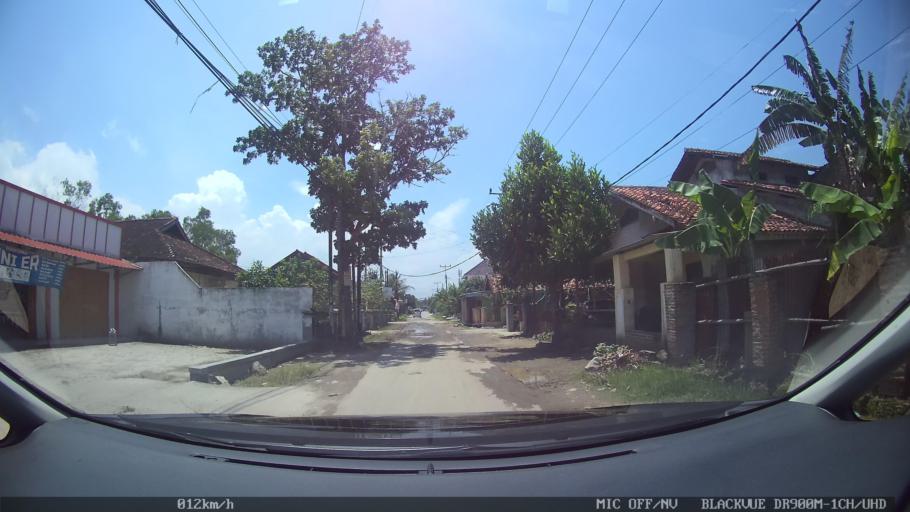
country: ID
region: Lampung
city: Kedaton
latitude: -5.3764
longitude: 105.2858
